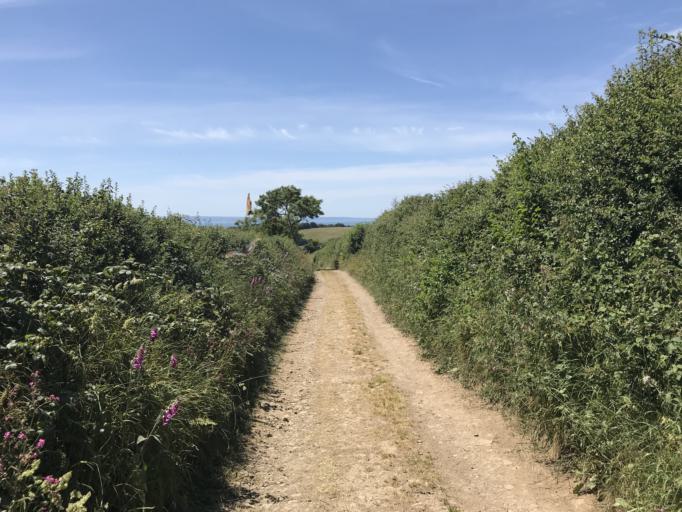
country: GB
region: England
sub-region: Devon
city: Braunton
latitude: 51.1184
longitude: -4.1535
